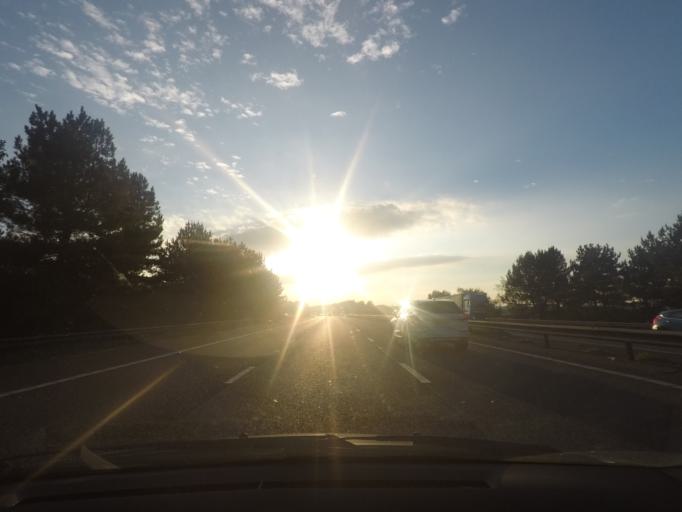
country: GB
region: England
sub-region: North Lincolnshire
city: Worlaby
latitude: 53.5769
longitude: -0.4581
